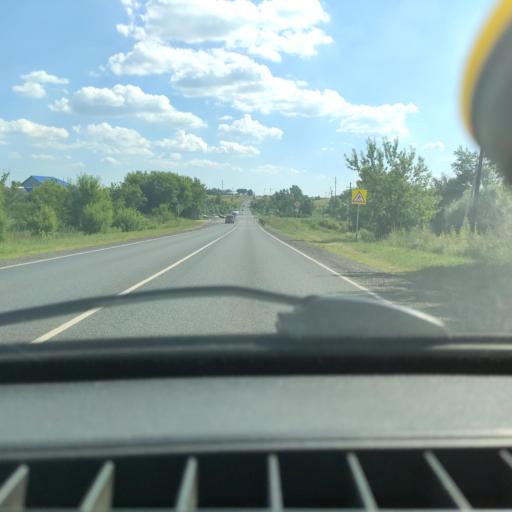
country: RU
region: Samara
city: Povolzhskiy
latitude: 53.7118
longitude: 49.7470
